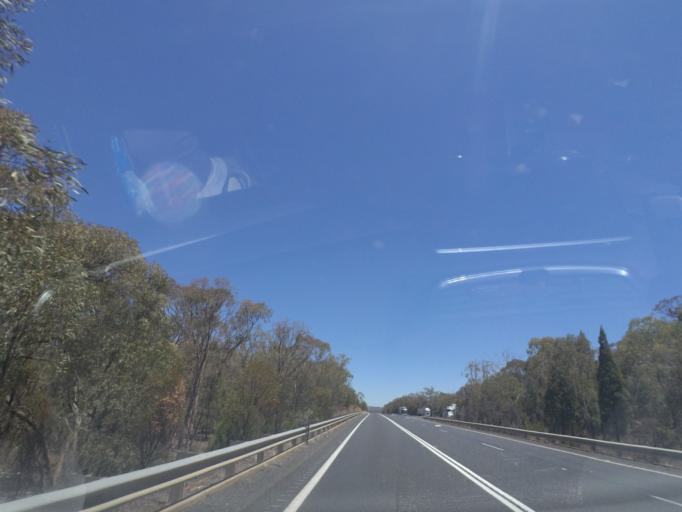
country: AU
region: New South Wales
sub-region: Warrumbungle Shire
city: Coonabarabran
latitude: -31.2314
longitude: 149.3191
